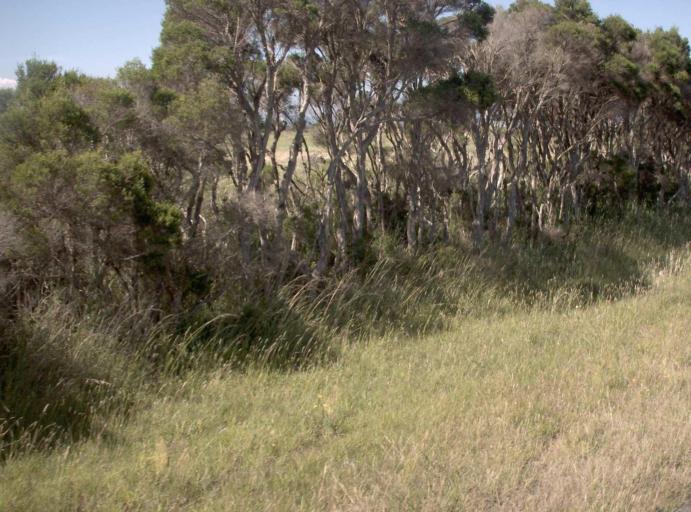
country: AU
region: Victoria
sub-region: Latrobe
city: Traralgon
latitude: -38.6319
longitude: 146.5909
